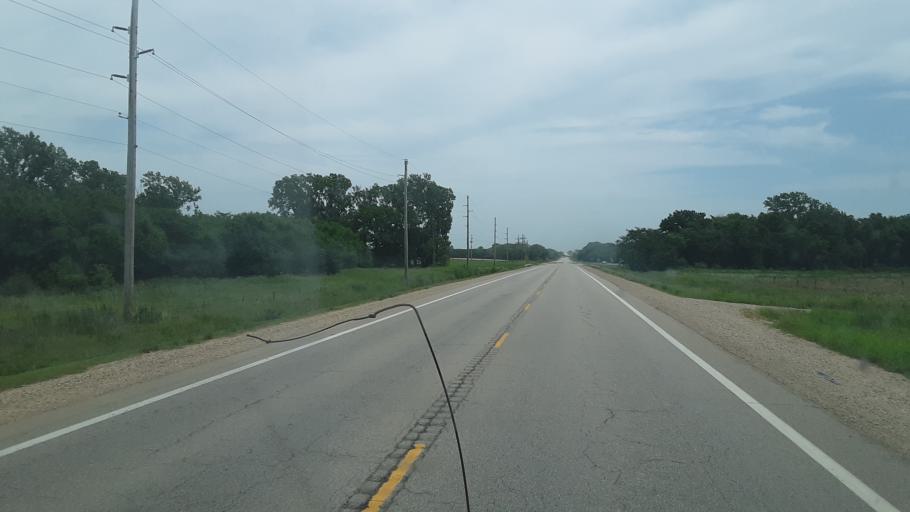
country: US
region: Kansas
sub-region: Woodson County
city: Yates Center
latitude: 37.8369
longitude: -95.9927
